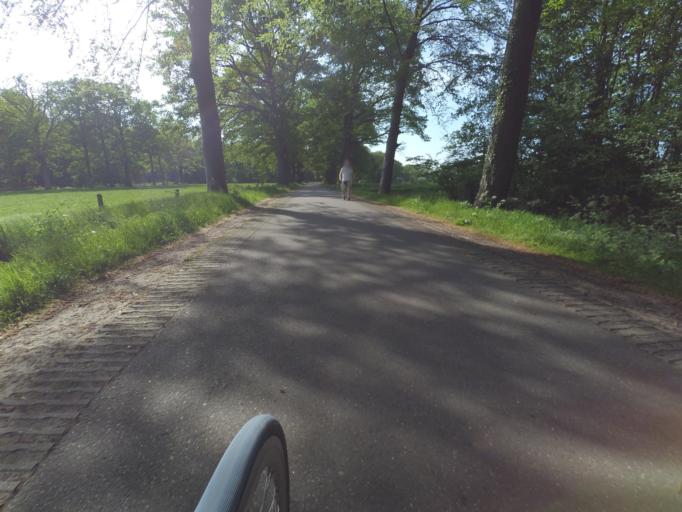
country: NL
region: Overijssel
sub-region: Gemeente Oldenzaal
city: Oldenzaal
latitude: 52.3773
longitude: 6.9765
